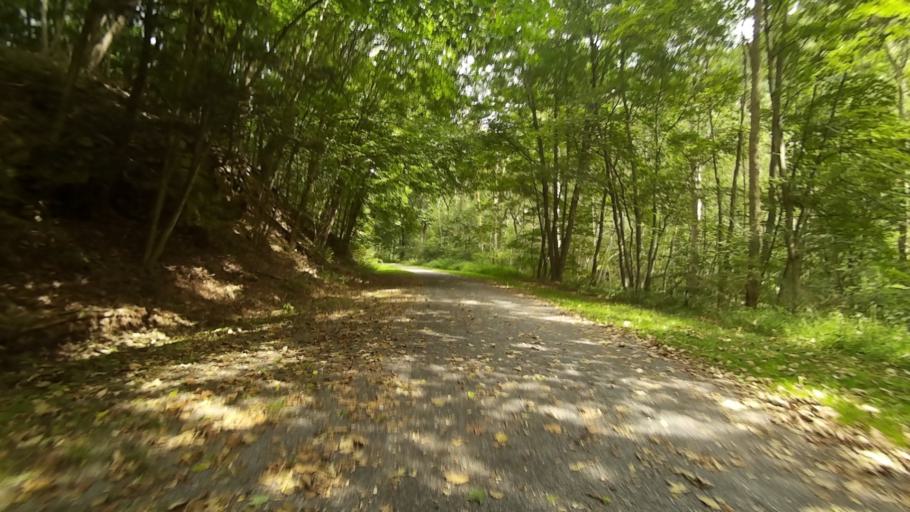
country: US
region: Pennsylvania
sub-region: Blair County
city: Williamsburg
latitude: 40.5419
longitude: -78.1502
